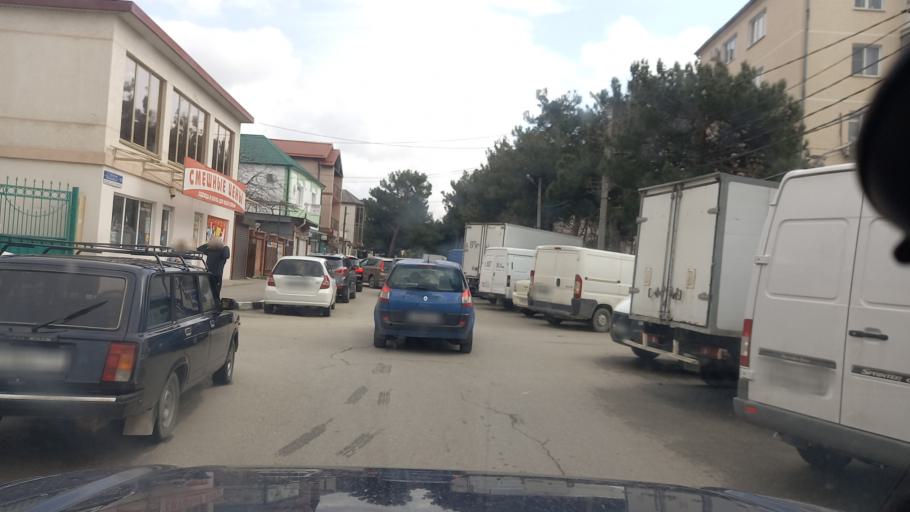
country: RU
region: Krasnodarskiy
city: Gelendzhik
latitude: 44.5621
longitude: 38.0819
